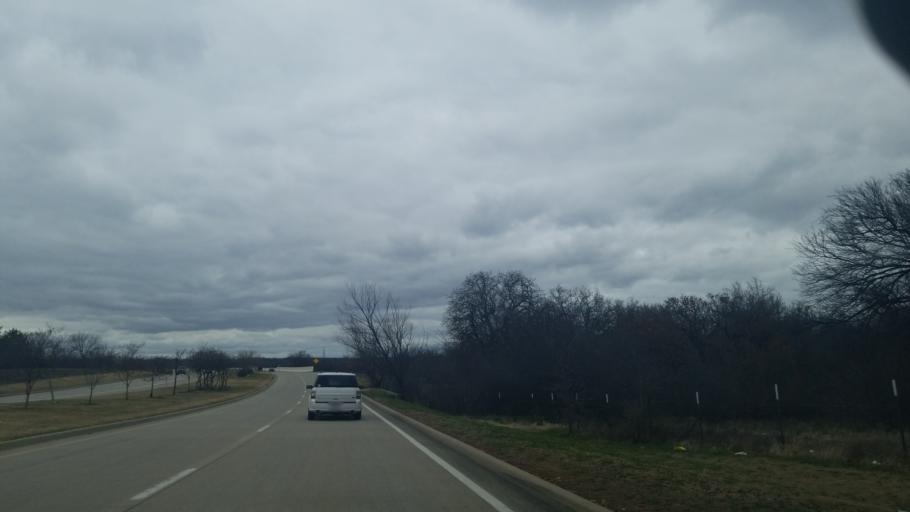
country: US
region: Texas
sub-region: Denton County
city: Copper Canyon
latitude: 33.1155
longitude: -97.0788
